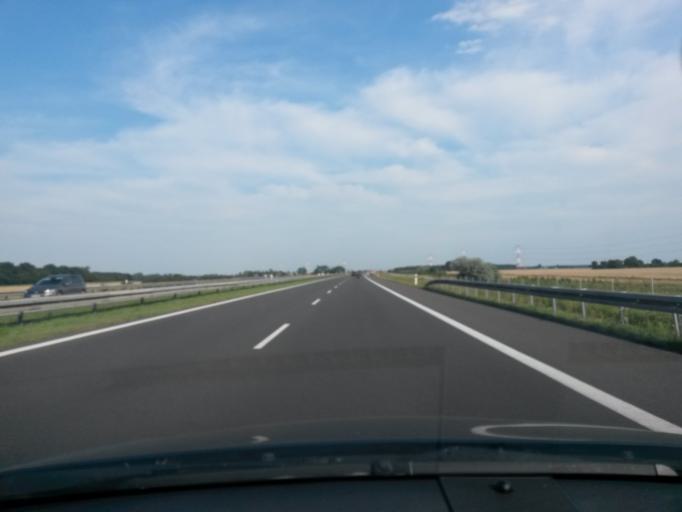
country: PL
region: Greater Poland Voivodeship
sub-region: Powiat wrzesinski
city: Kolaczkowo
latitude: 52.2896
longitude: 17.6698
